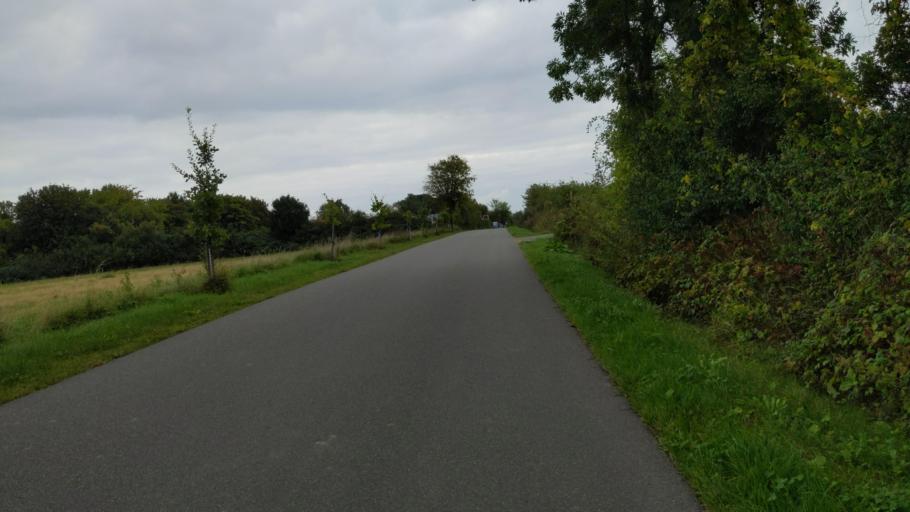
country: DE
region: Schleswig-Holstein
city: Buchholz
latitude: 53.7582
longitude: 10.7640
